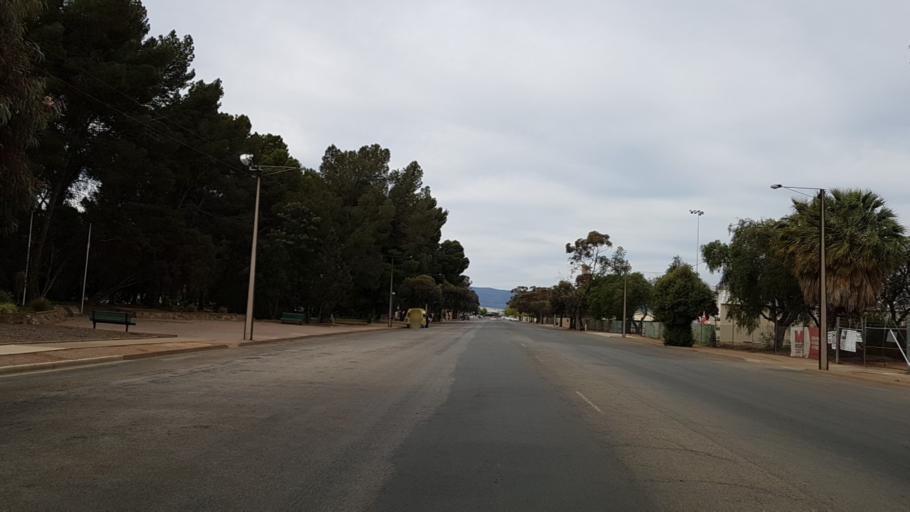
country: AU
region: South Australia
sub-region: Port Pirie City and Dists
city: Port Pirie
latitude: -33.1808
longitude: 138.0050
